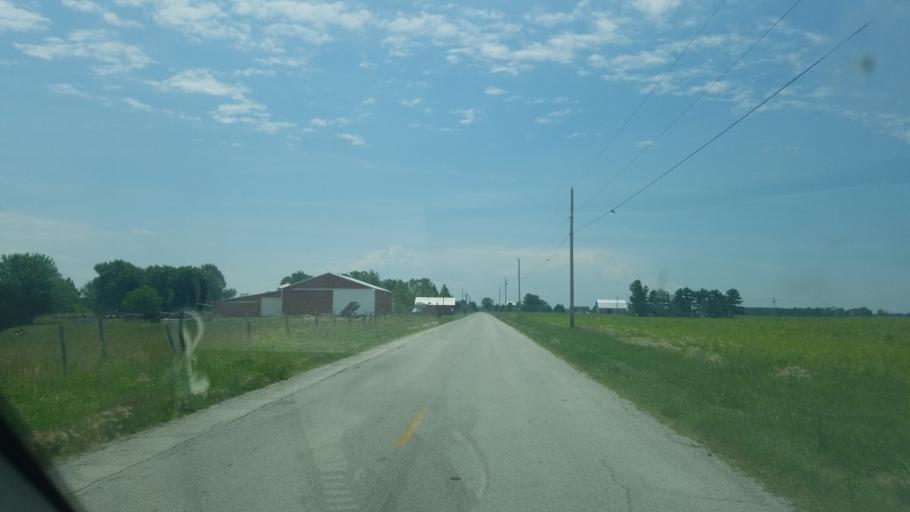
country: US
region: Ohio
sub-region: Wood County
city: North Baltimore
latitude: 41.2142
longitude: -83.5924
